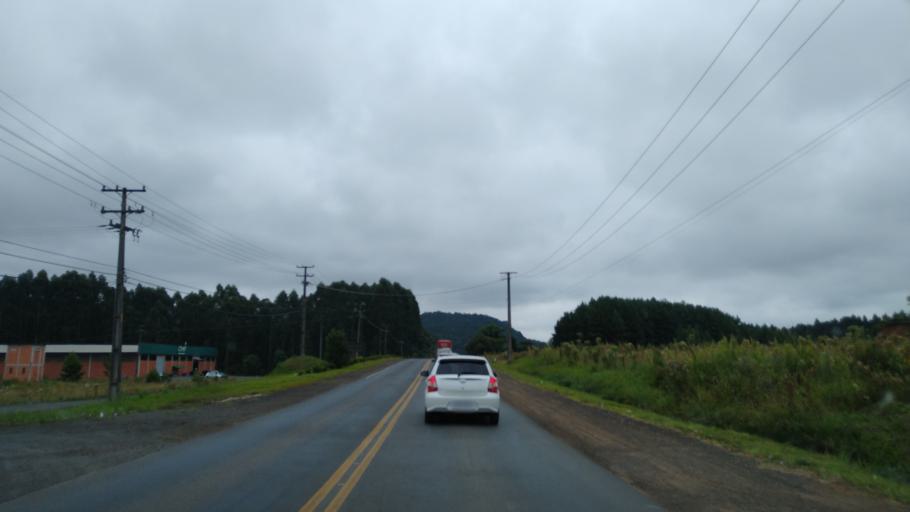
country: BR
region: Parana
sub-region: Uniao Da Vitoria
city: Uniao da Vitoria
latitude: -26.2414
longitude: -51.1236
